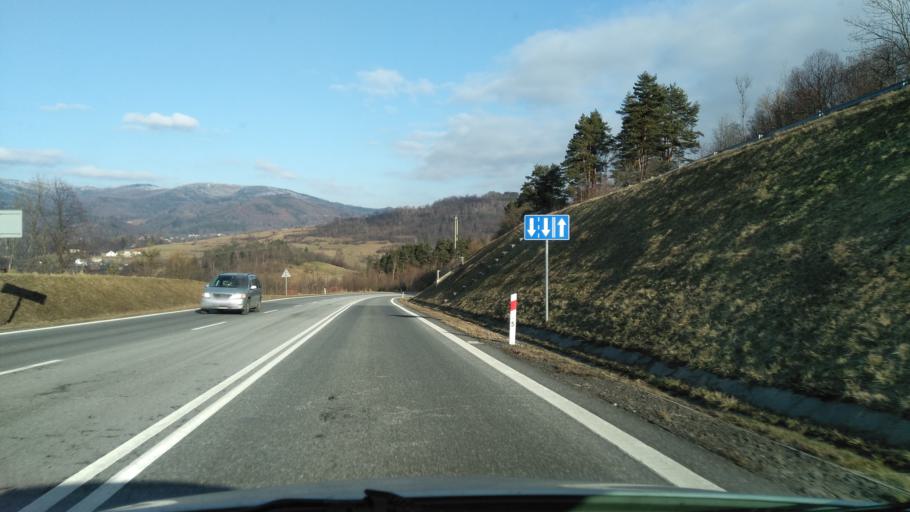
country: PL
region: Silesian Voivodeship
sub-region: Powiat zywiecki
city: Milowka
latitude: 49.5605
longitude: 19.0623
